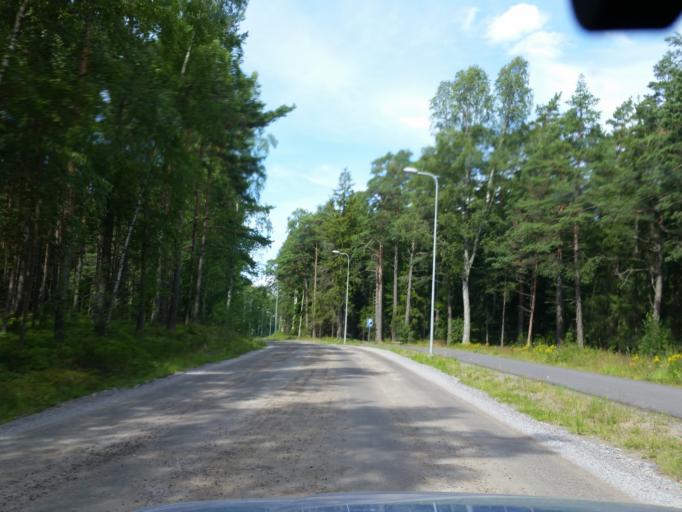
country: FI
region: Uusimaa
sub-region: Raaseporin
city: Hanko
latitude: 59.8389
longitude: 22.9535
